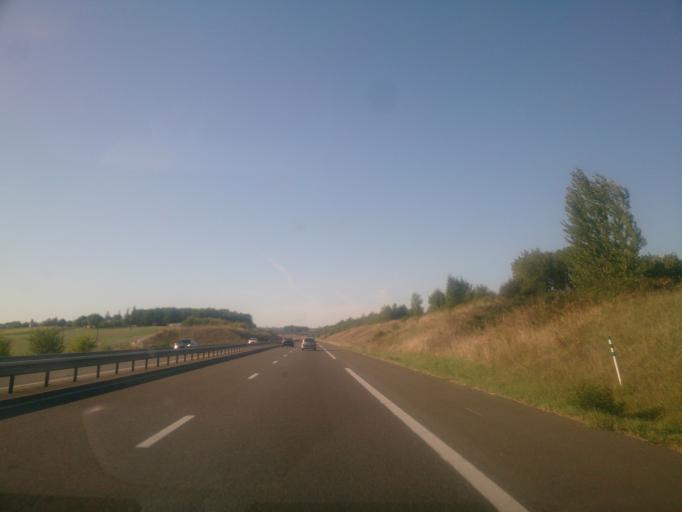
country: FR
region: Midi-Pyrenees
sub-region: Departement du Tarn-et-Garonne
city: Caussade
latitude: 44.2144
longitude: 1.5408
